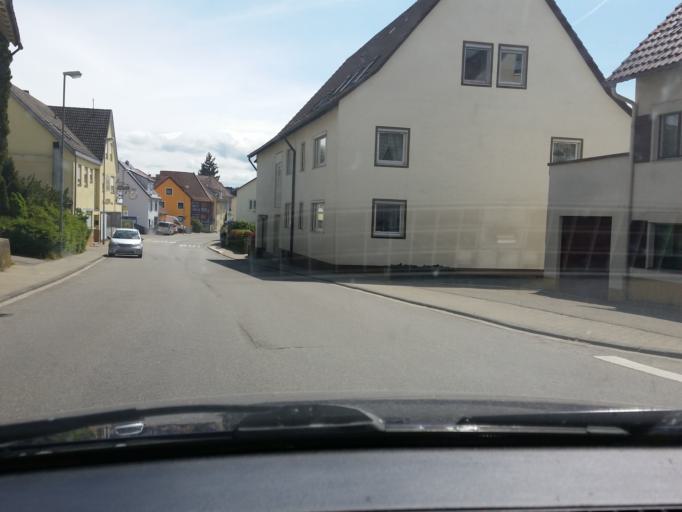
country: DE
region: Baden-Wuerttemberg
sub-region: Freiburg Region
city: Allensbach
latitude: 47.7370
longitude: 9.1164
